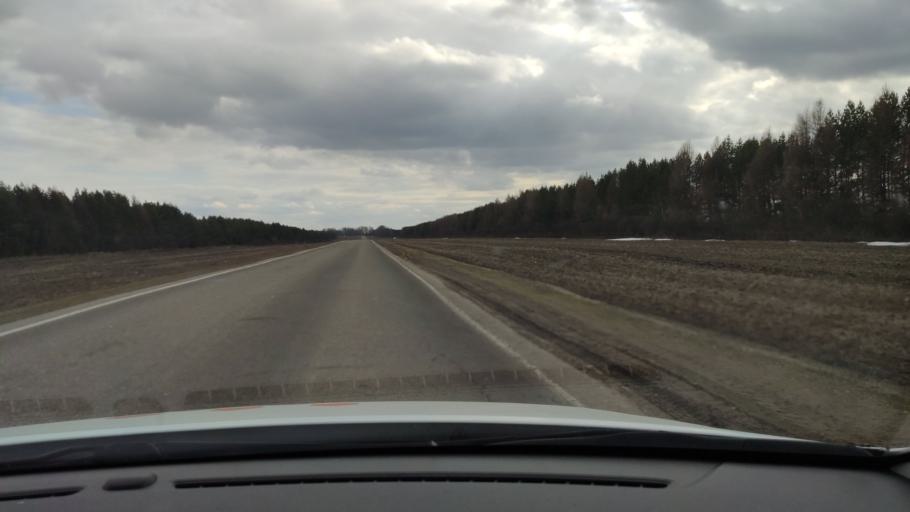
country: RU
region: Tatarstan
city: Vysokaya Gora
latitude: 56.1495
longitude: 49.2115
